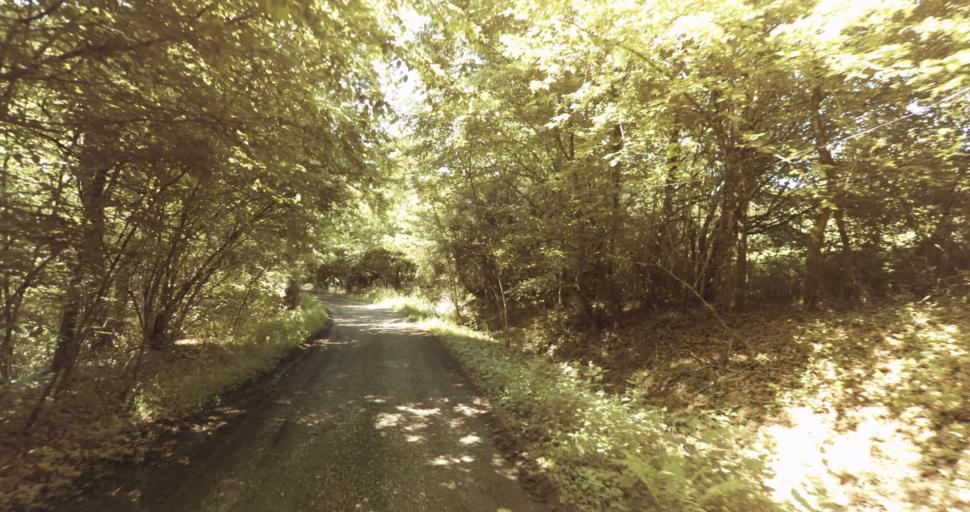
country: FR
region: Limousin
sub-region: Departement de la Haute-Vienne
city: Le Vigen
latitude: 45.7261
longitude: 1.3031
